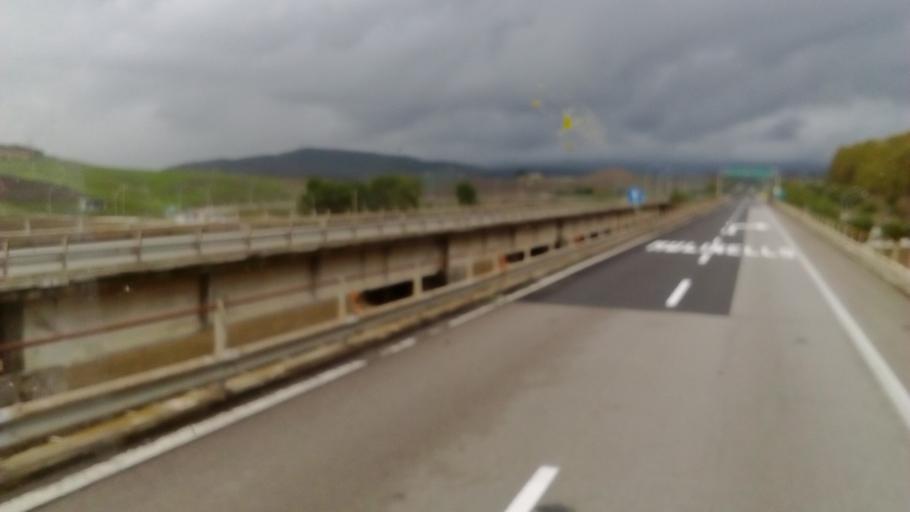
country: IT
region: Sicily
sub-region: Enna
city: Assoro
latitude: 37.5663
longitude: 14.4050
